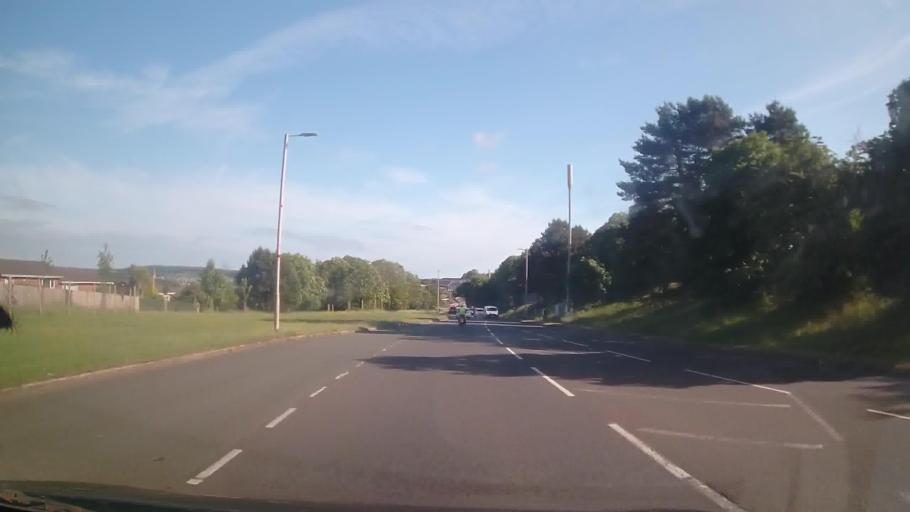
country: GB
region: England
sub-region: Devon
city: Plympton
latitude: 50.4104
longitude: -4.0946
